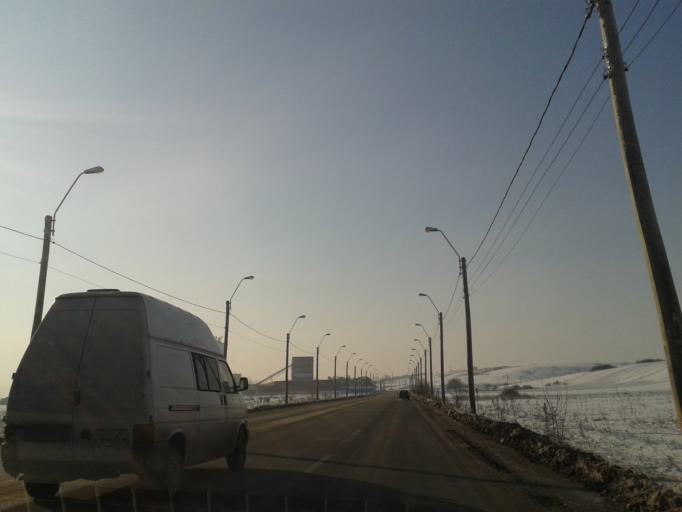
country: RO
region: Hunedoara
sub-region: Municipiul Deva
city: Cristur
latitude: 45.8480
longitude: 22.9524
